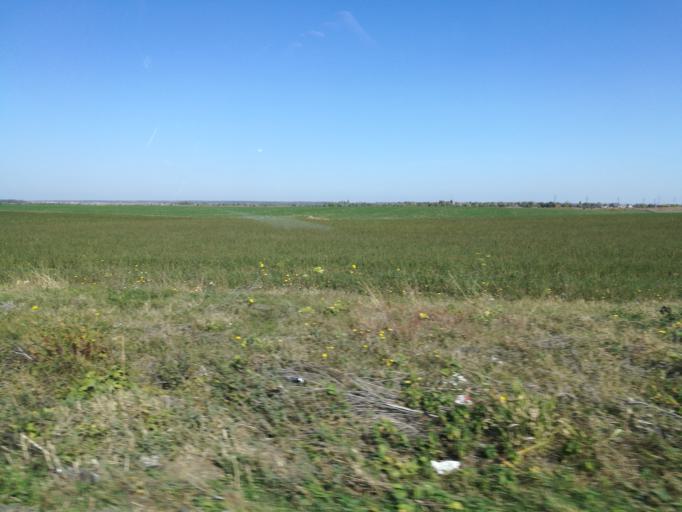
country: RO
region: Giurgiu
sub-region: Comuna Joita
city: Bacu
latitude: 44.4781
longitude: 25.9022
